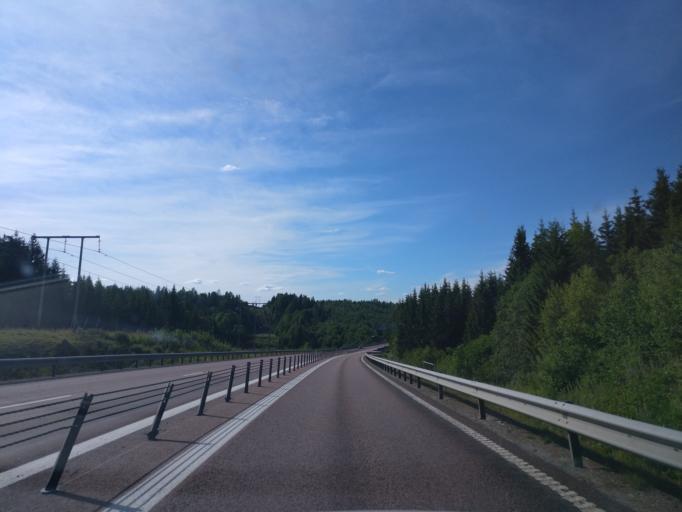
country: SE
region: Vaermland
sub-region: Kils Kommun
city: Kil
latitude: 59.5023
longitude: 13.2601
